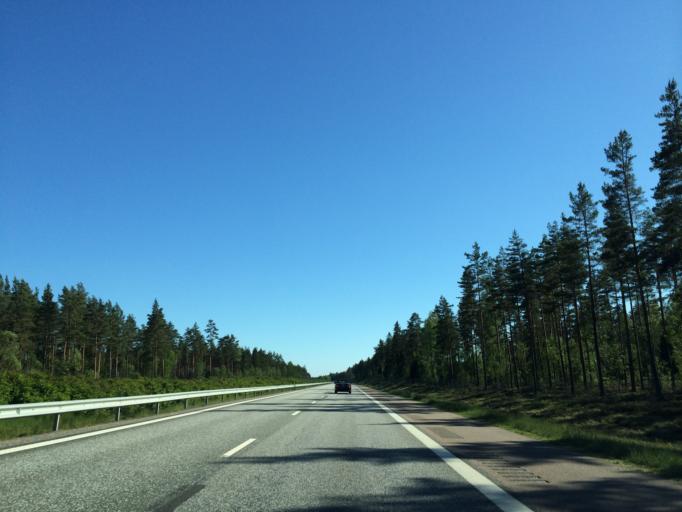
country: SE
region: Joenkoeping
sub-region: Vaggeryds Kommun
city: Skillingaryd
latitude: 57.4003
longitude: 14.0999
